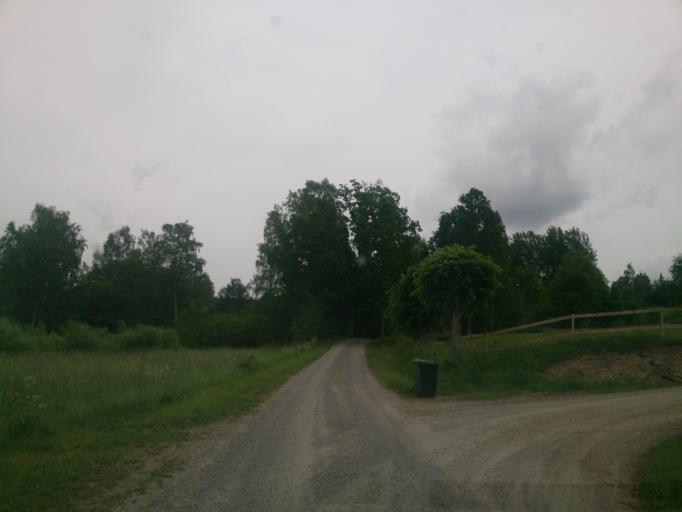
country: SE
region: OEstergoetland
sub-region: Valdemarsviks Kommun
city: Gusum
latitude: 58.3143
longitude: 16.4622
